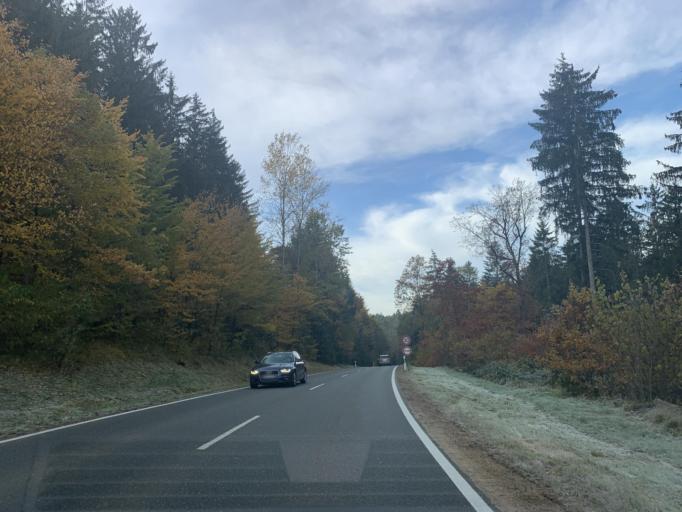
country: DE
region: Bavaria
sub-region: Upper Palatinate
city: Bach
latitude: 49.3846
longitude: 12.3857
